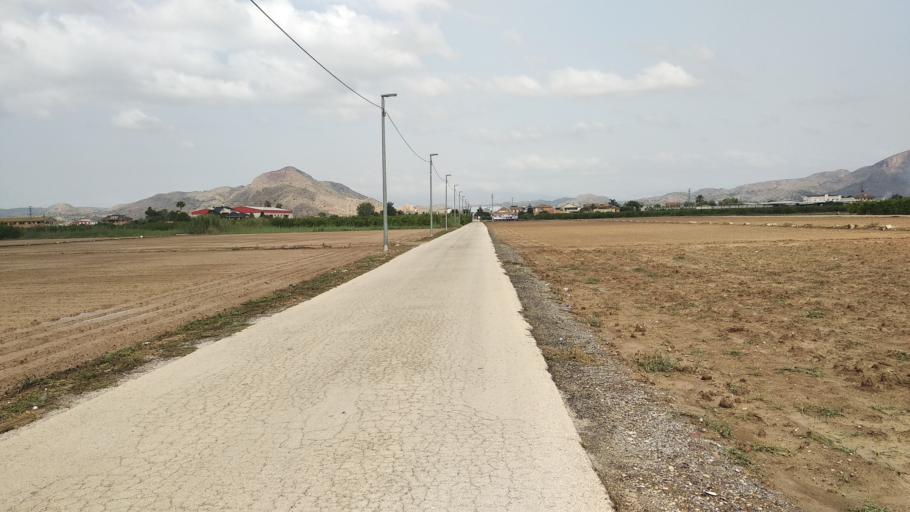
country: ES
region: Murcia
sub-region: Murcia
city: Santomera
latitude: 38.0388
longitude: -1.0392
